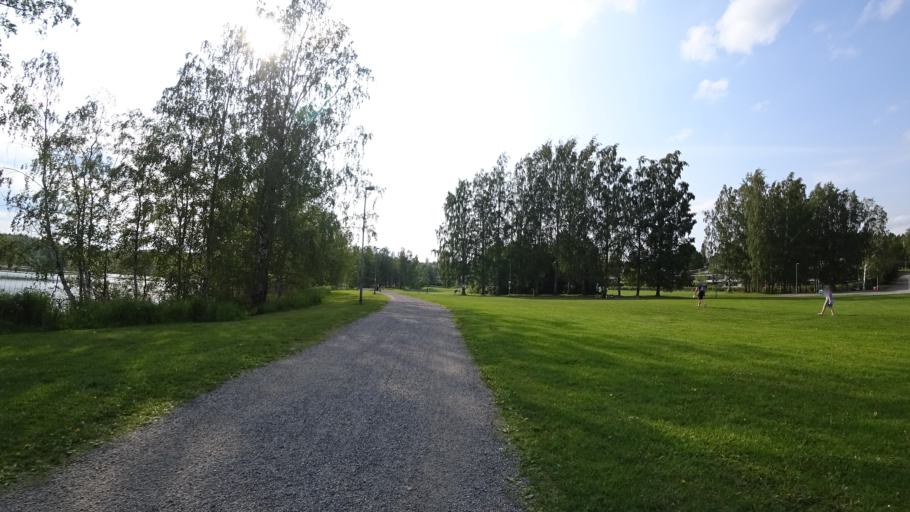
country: FI
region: Pirkanmaa
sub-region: Tampere
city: Pirkkala
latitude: 61.5057
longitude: 23.6724
